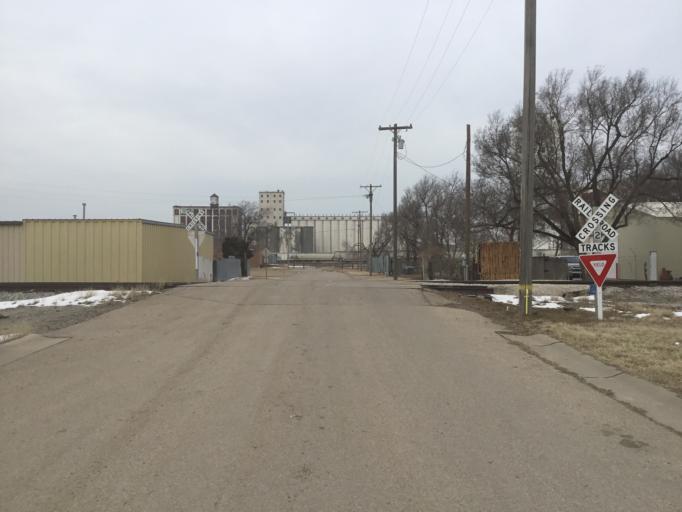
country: US
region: Kansas
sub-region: Sedgwick County
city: Wichita
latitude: 37.7190
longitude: -97.3286
